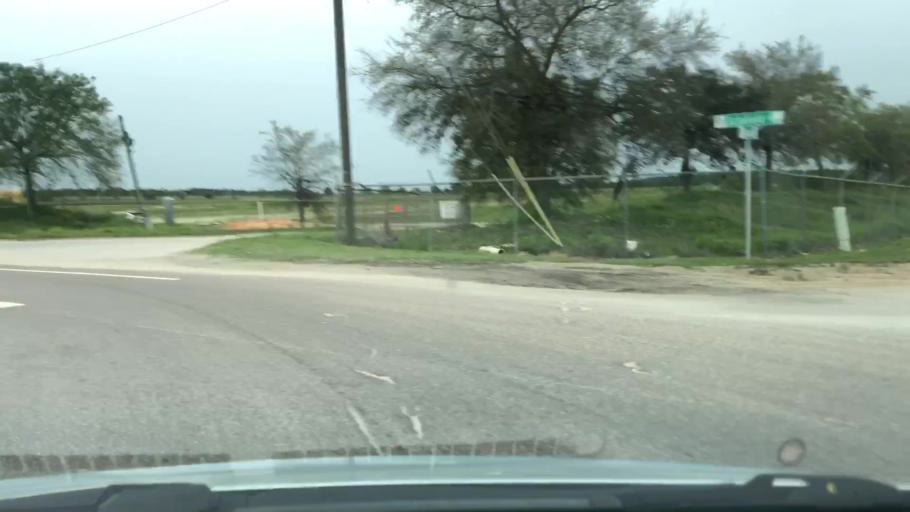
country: US
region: Florida
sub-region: Orange County
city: Oakland
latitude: 28.4490
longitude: -81.6363
